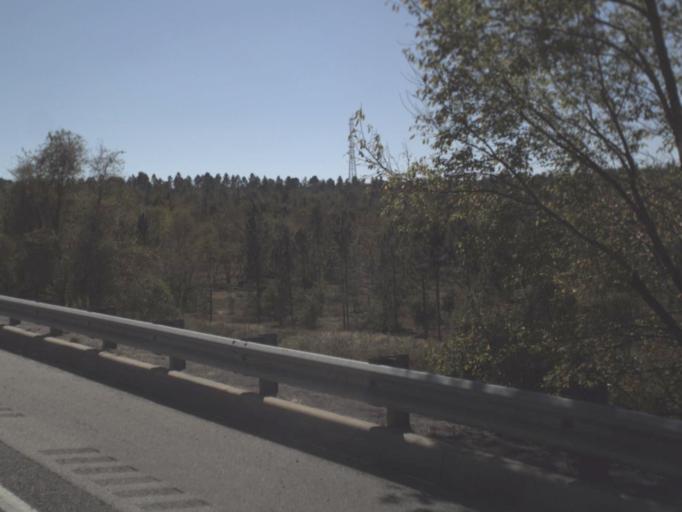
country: US
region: Florida
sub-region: Lake County
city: Minneola
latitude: 28.6075
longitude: -81.7260
